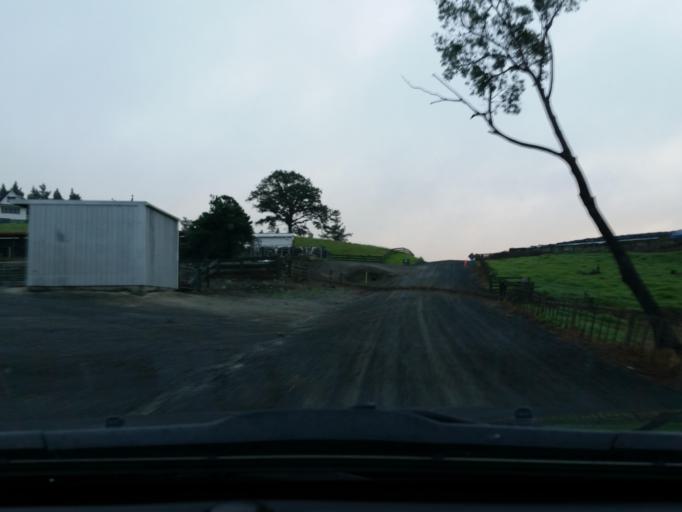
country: NZ
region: Northland
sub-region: Kaipara District
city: Dargaville
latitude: -35.8756
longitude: 174.0218
